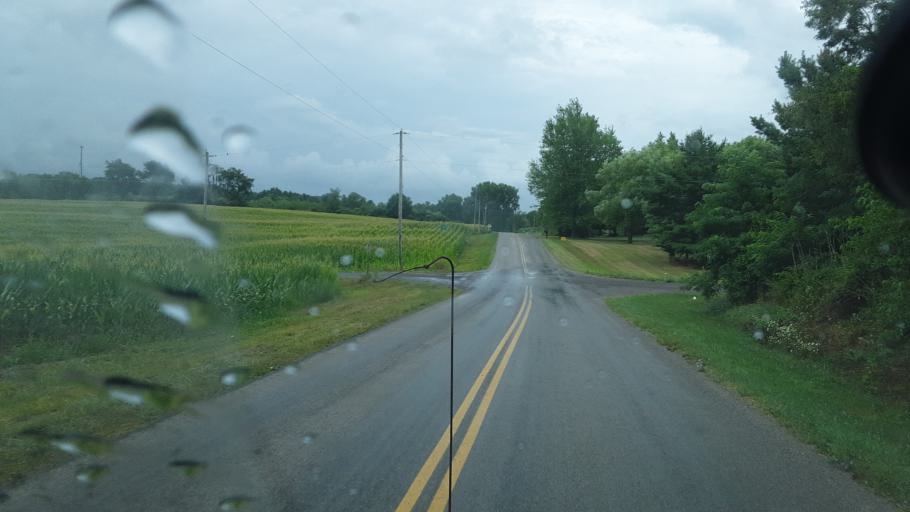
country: US
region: Indiana
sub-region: Steuben County
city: Hamilton
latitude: 41.6428
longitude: -84.7910
